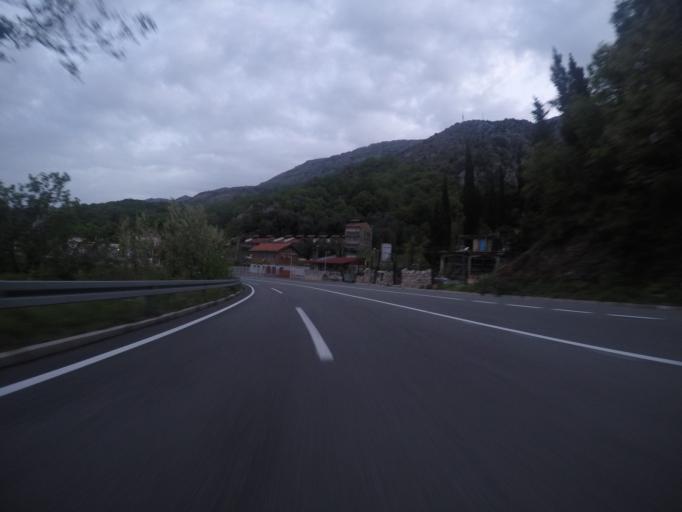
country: ME
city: Petrovac na Moru
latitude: 42.1961
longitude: 18.9829
